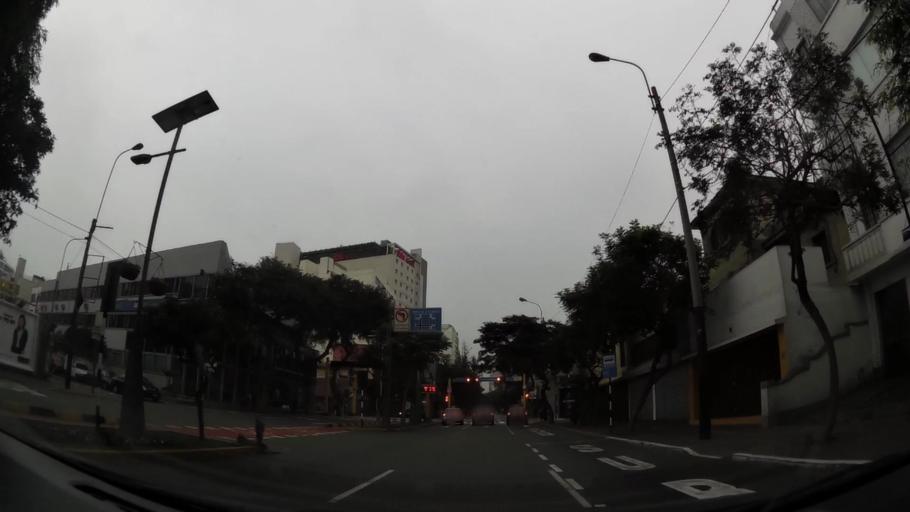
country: PE
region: Lima
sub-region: Lima
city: San Isidro
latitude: -12.1303
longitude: -77.0298
